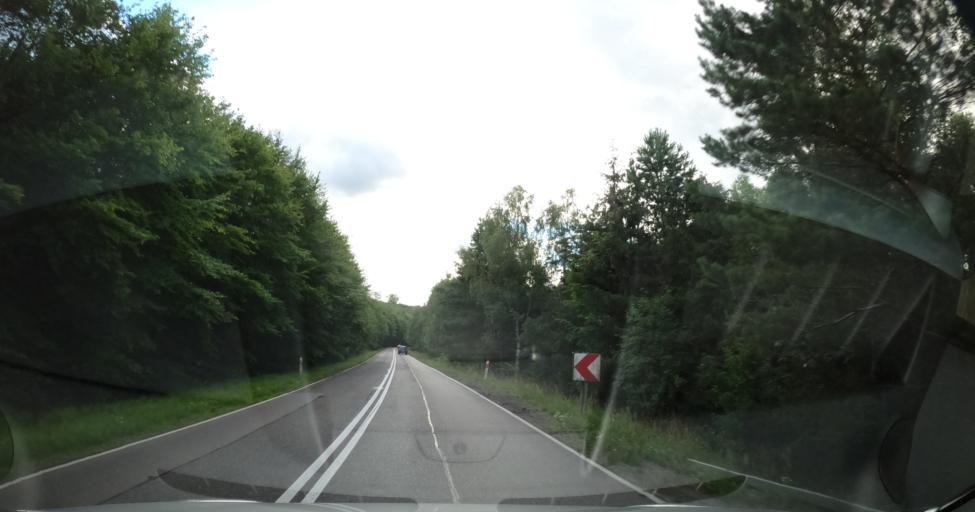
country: PL
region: Pomeranian Voivodeship
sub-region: Powiat bytowski
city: Czarna Dabrowka
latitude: 54.3752
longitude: 17.4986
